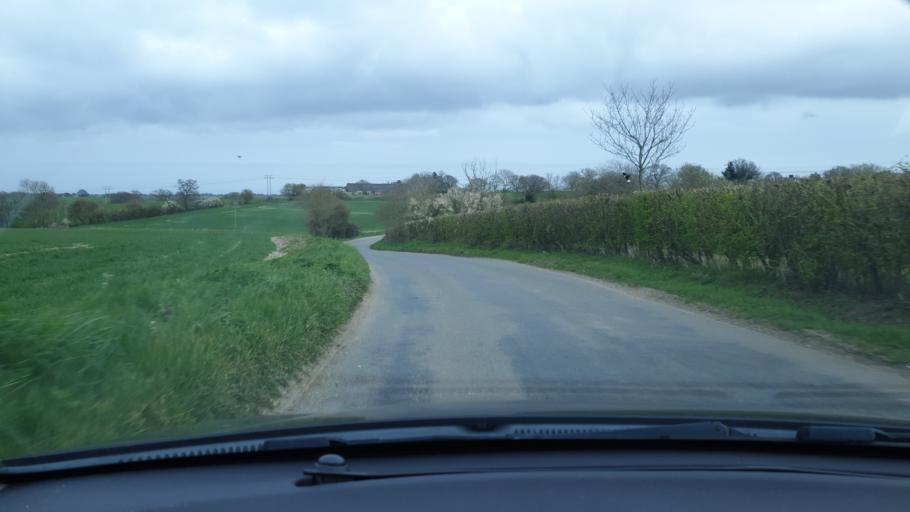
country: GB
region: England
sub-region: Essex
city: Mistley
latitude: 51.9297
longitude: 1.1756
